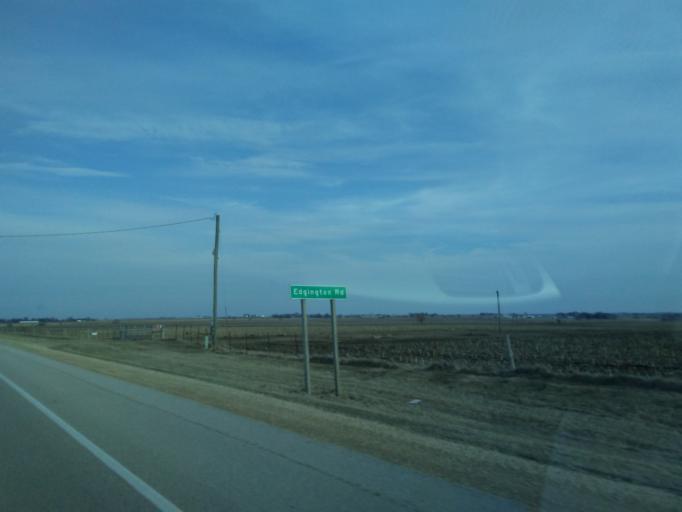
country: US
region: Wisconsin
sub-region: Iowa County
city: Mineral Point
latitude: 42.9669
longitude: -90.3625
